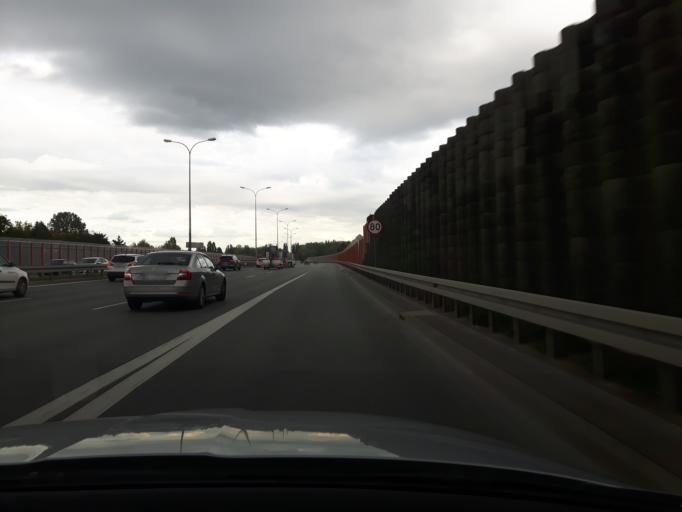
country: PL
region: Masovian Voivodeship
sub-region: Warszawa
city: Mokotow
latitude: 52.2035
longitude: 21.0738
